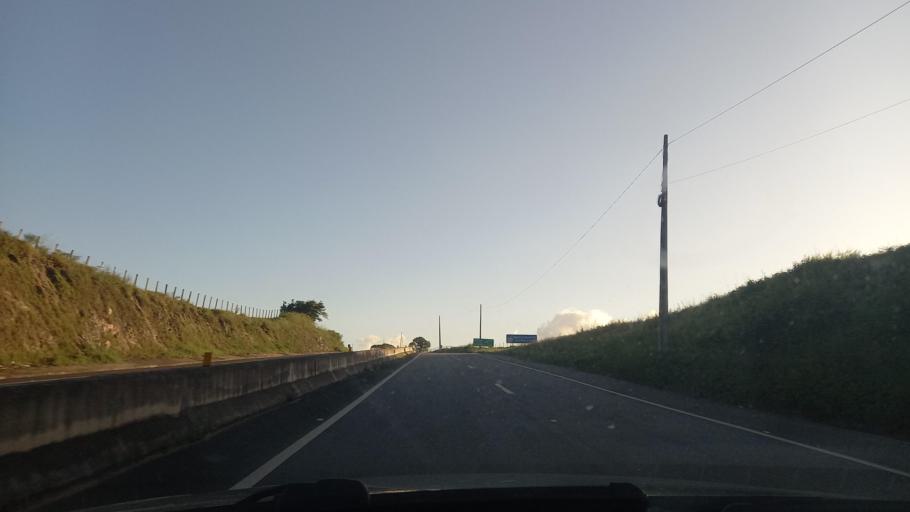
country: BR
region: Alagoas
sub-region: Limoeiro De Anadia
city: Limoeiro de Anadia
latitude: -9.7421
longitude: -36.4980
